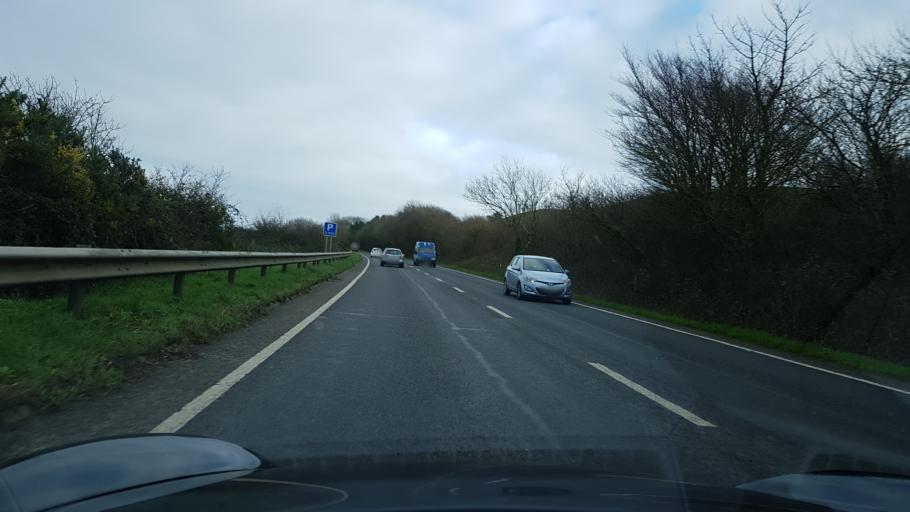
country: GB
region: England
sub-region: Dorset
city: Bridport
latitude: 50.7277
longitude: -2.6700
